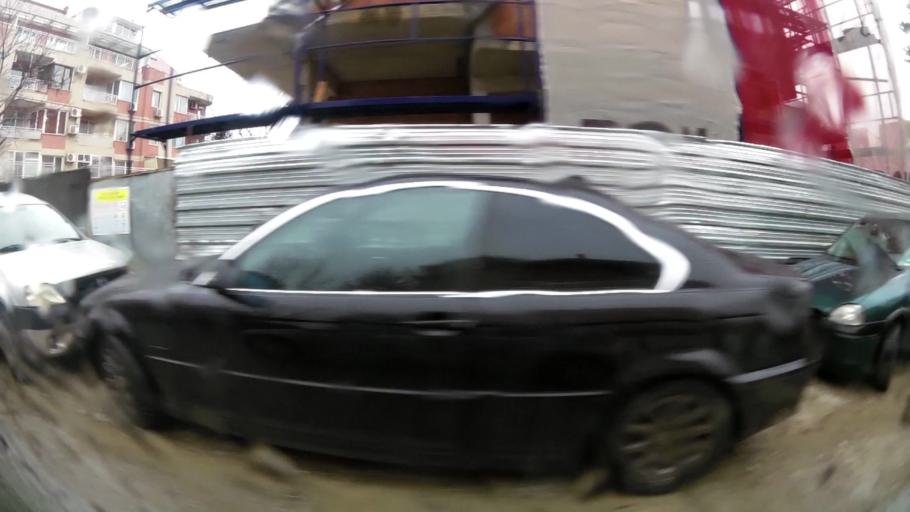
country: BG
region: Sofia-Capital
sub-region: Stolichna Obshtina
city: Sofia
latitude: 42.6458
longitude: 23.3319
